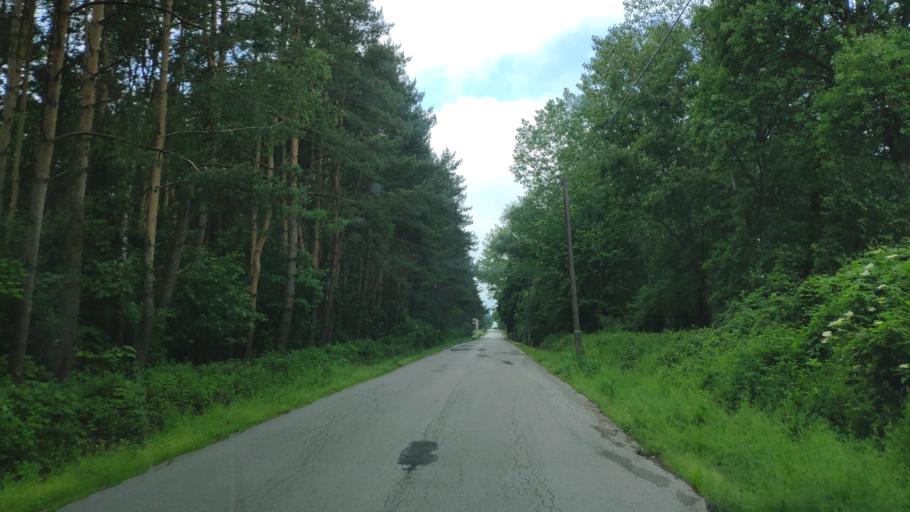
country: SK
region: Presovsky
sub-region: Okres Presov
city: Presov
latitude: 48.9996
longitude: 21.3149
